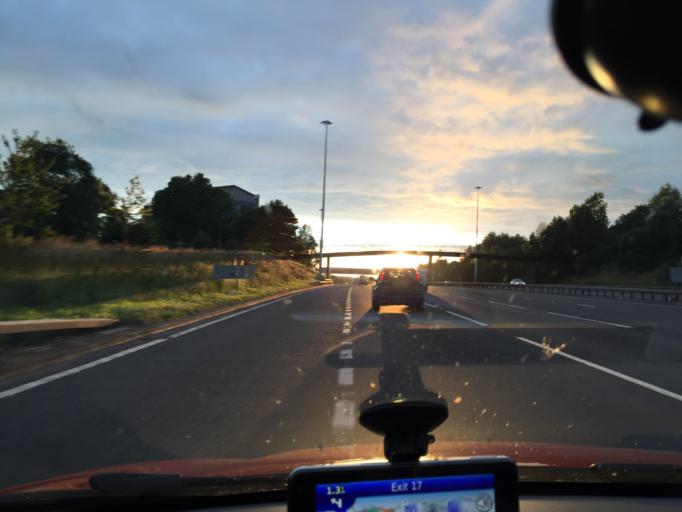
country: GB
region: Scotland
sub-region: Glasgow City
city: Glasgow
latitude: 55.8692
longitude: -4.2422
